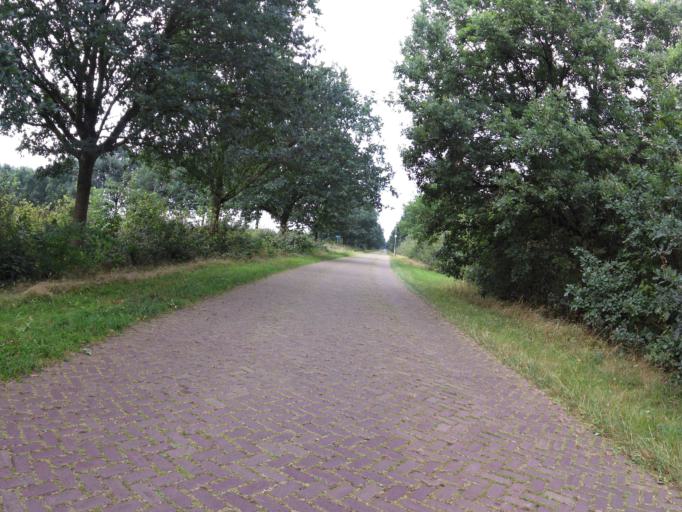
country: NL
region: Drenthe
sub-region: Gemeente Emmen
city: Klazienaveen
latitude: 52.6738
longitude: 6.9625
